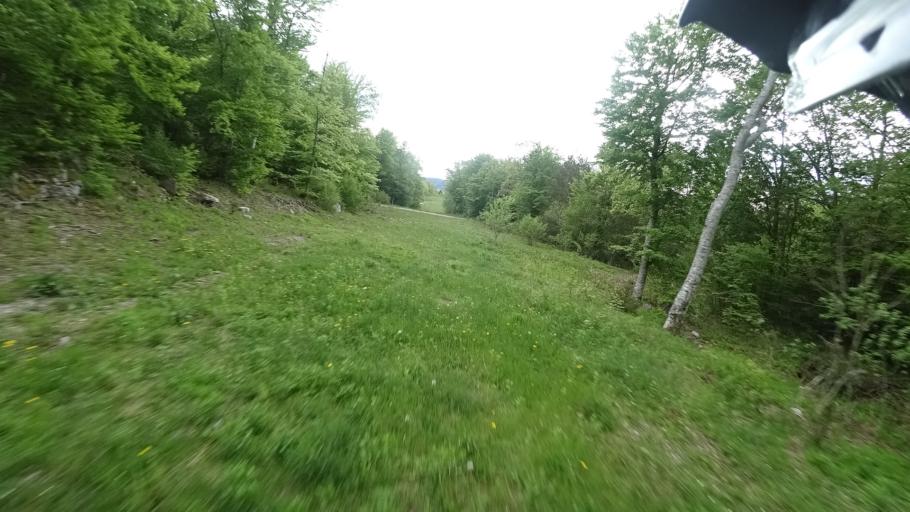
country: HR
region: Karlovacka
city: Plaski
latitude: 44.9061
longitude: 15.4165
